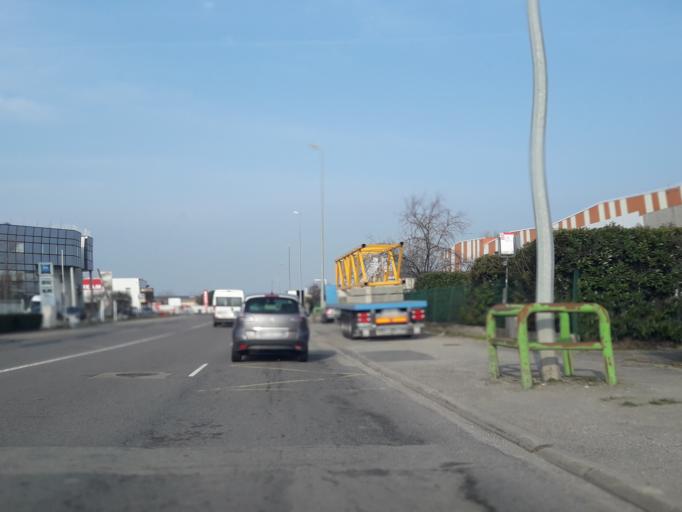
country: FR
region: Rhone-Alpes
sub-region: Departement du Rhone
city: Chassieu
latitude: 45.7258
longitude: 4.9699
